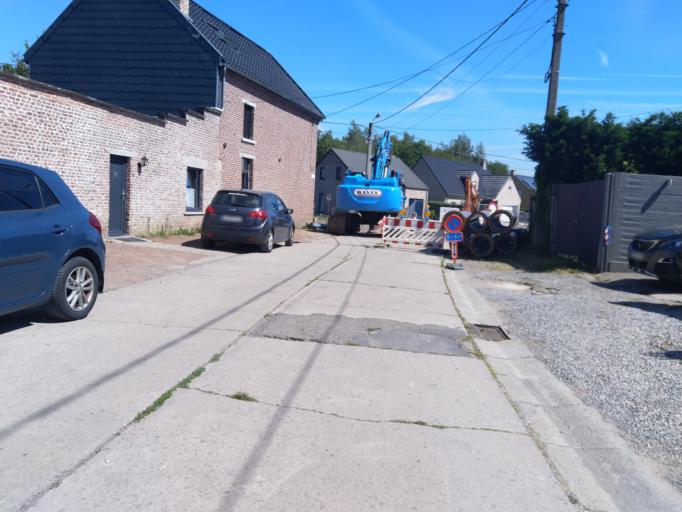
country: BE
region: Wallonia
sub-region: Province du Hainaut
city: Colfontaine
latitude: 50.4192
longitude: 3.8678
